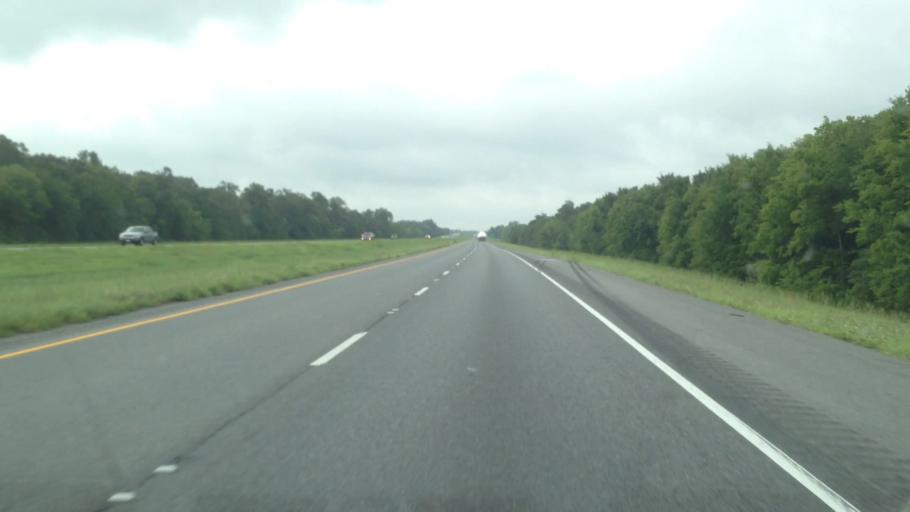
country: US
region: Louisiana
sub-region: Saint Landry Parish
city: Opelousas
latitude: 30.6633
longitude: -92.0683
